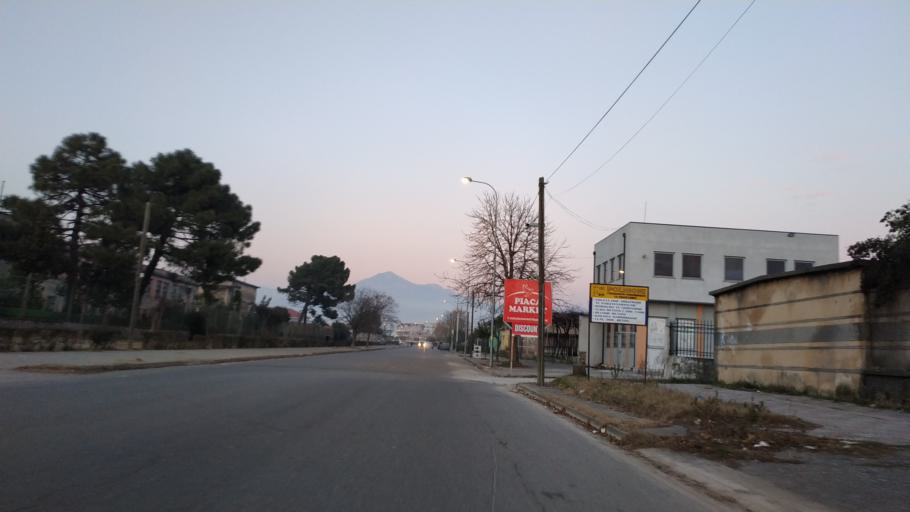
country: AL
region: Shkoder
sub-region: Rrethi i Shkodres
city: Shkoder
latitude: 42.0797
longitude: 19.5282
